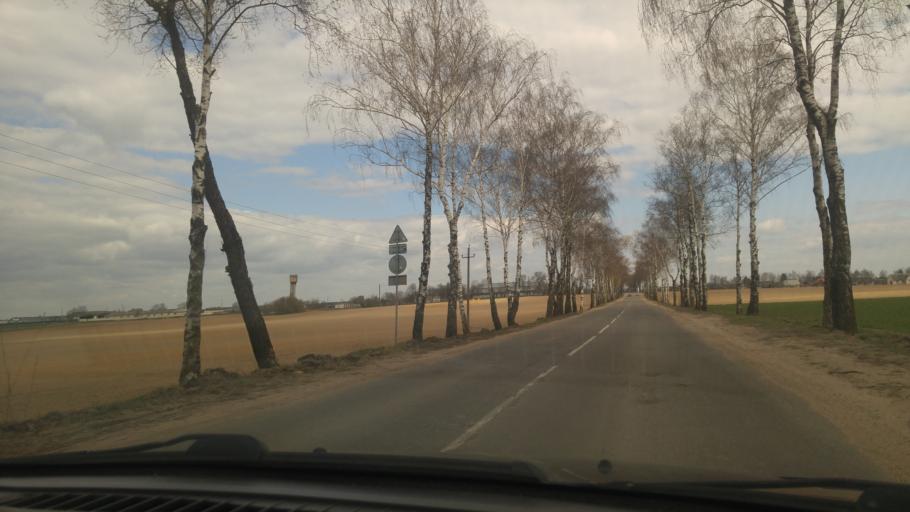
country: BY
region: Minsk
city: Rudzyensk
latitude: 53.6582
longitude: 27.7910
